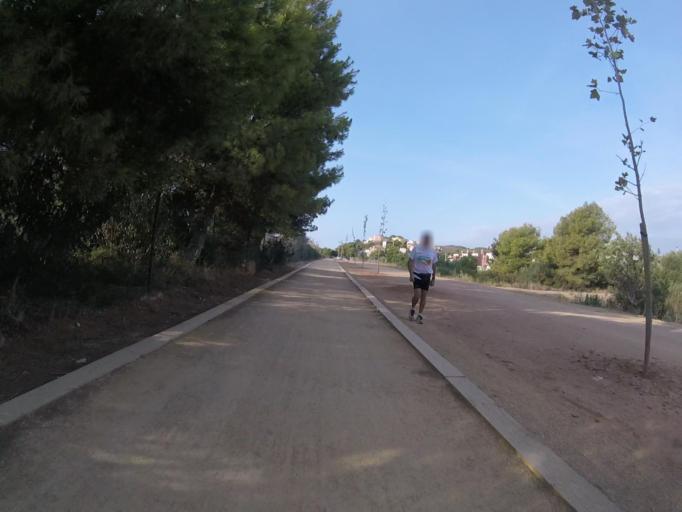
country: ES
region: Valencia
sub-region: Provincia de Castello
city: Orpesa/Oropesa del Mar
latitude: 40.0864
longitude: 0.1376
